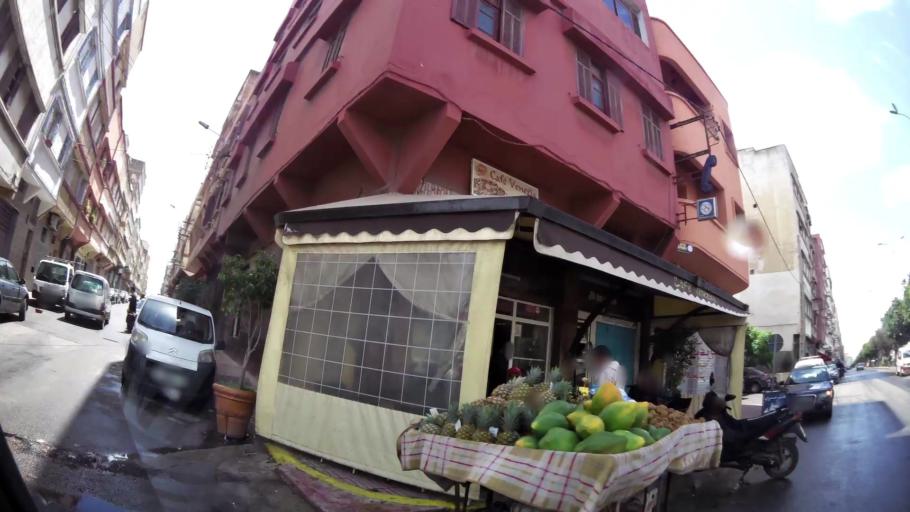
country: MA
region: Grand Casablanca
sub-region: Casablanca
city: Casablanca
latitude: 33.5781
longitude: -7.5906
